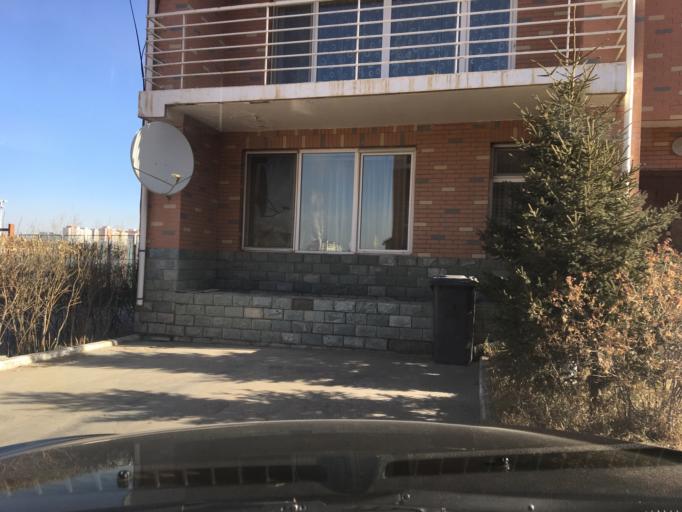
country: MN
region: Ulaanbaatar
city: Ulaanbaatar
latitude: 47.8886
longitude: 106.9085
